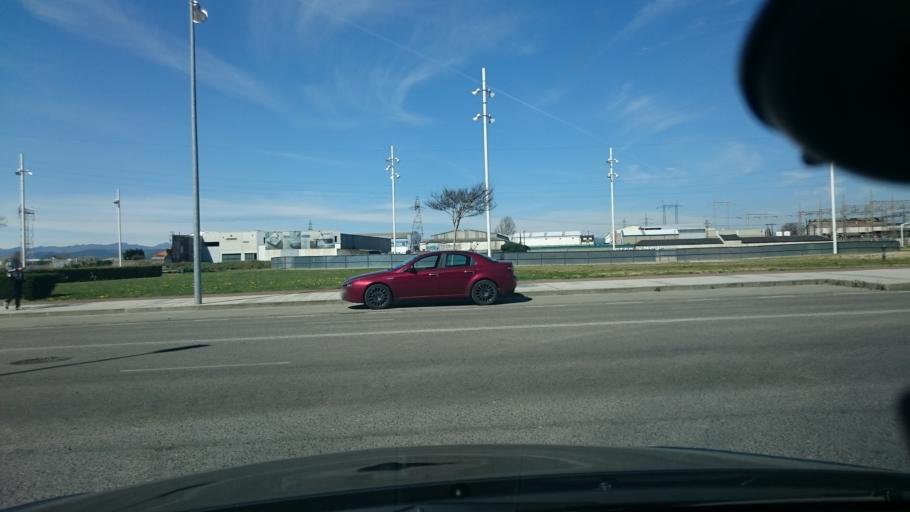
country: ES
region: Castille and Leon
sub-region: Provincia de Leon
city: Ponferrada
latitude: 42.5584
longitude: -6.6077
